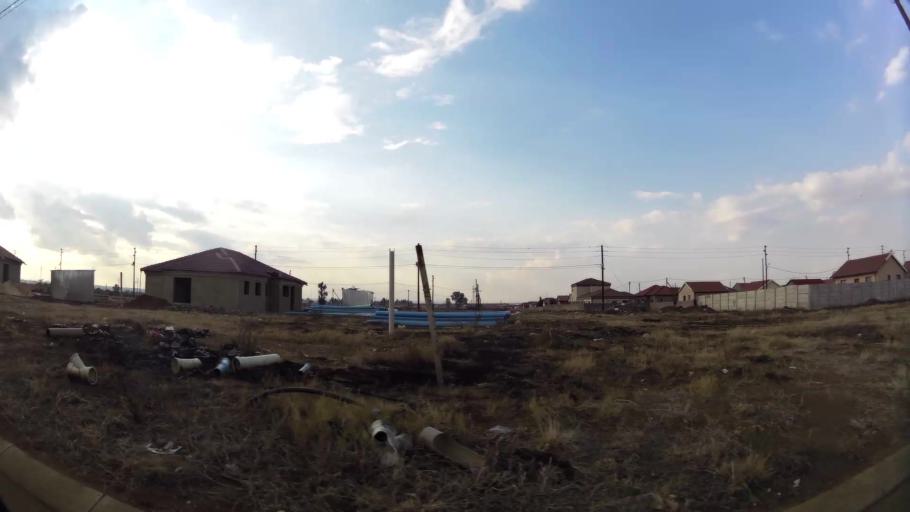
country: ZA
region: Gauteng
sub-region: Sedibeng District Municipality
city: Vanderbijlpark
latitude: -26.6101
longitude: 27.8111
